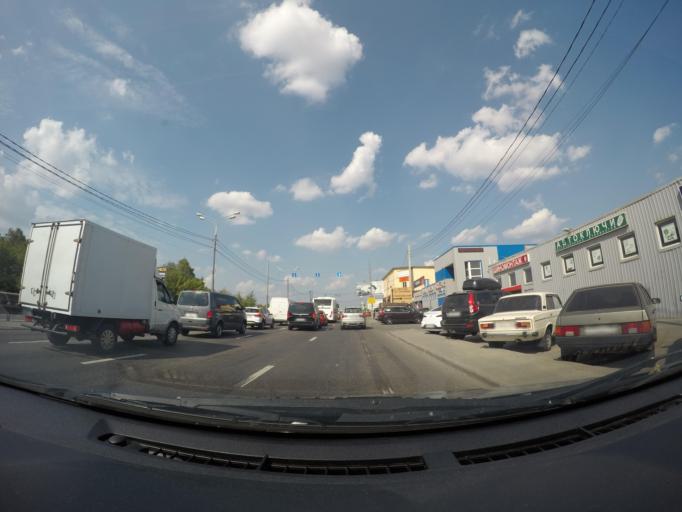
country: RU
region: Moskovskaya
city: Dolgoprudnyy
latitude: 55.9175
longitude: 37.4948
